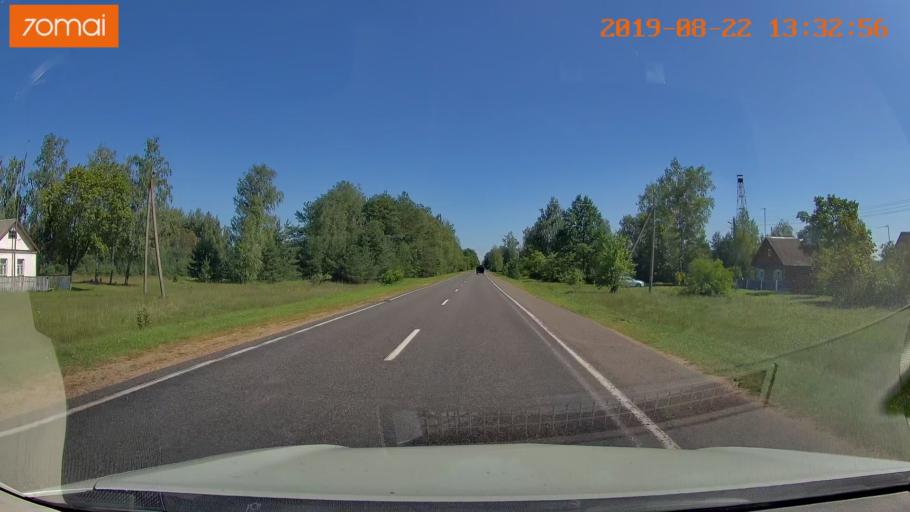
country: BY
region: Minsk
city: Staryya Darohi
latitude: 53.2169
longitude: 28.2158
